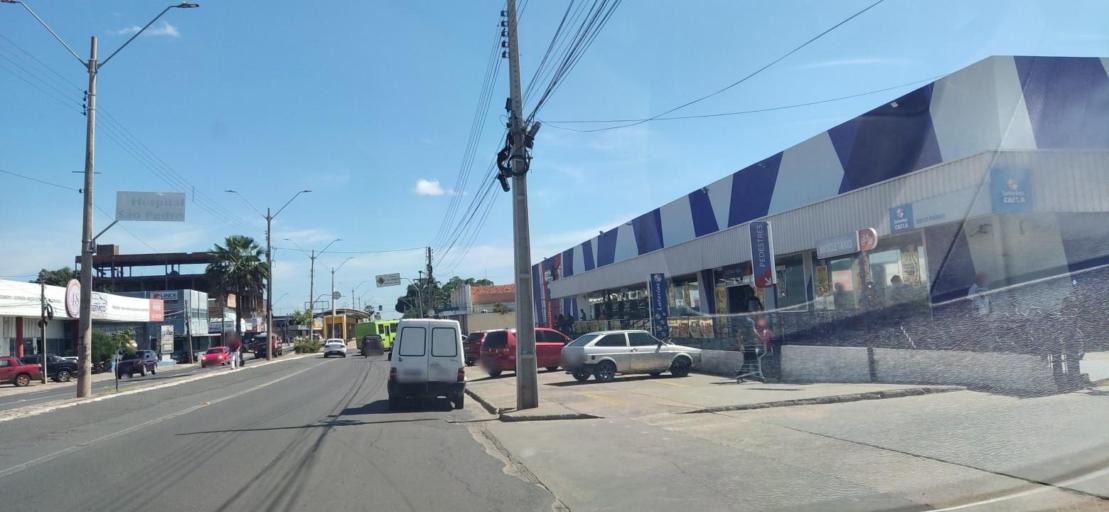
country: BR
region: Piaui
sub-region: Teresina
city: Teresina
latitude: -5.1186
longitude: -42.8034
